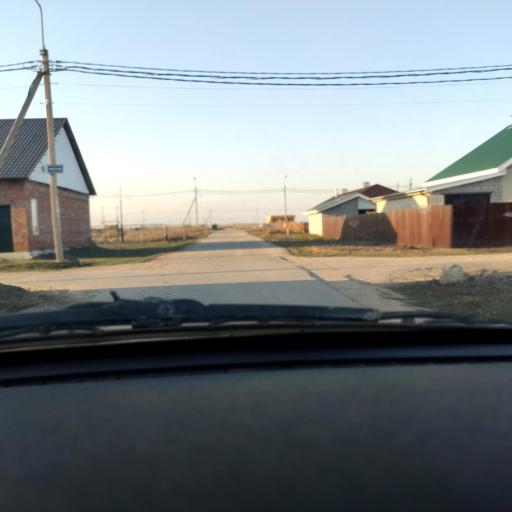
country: RU
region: Samara
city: Podstepki
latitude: 53.5756
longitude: 49.1136
